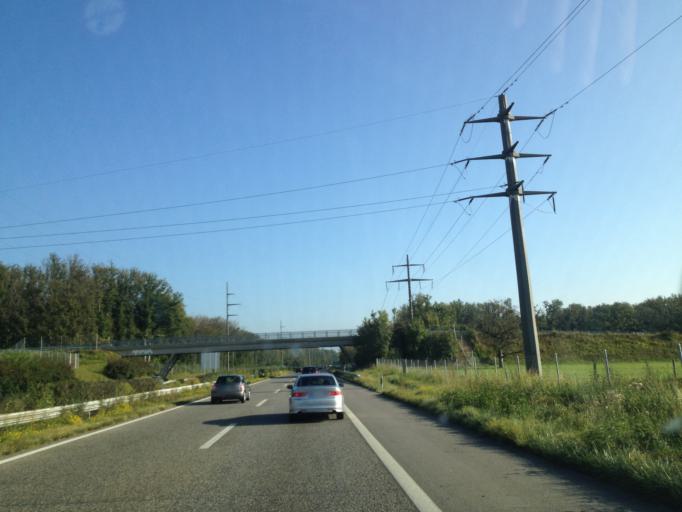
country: CH
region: Vaud
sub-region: Nyon District
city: Founex
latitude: 46.3471
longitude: 6.1696
